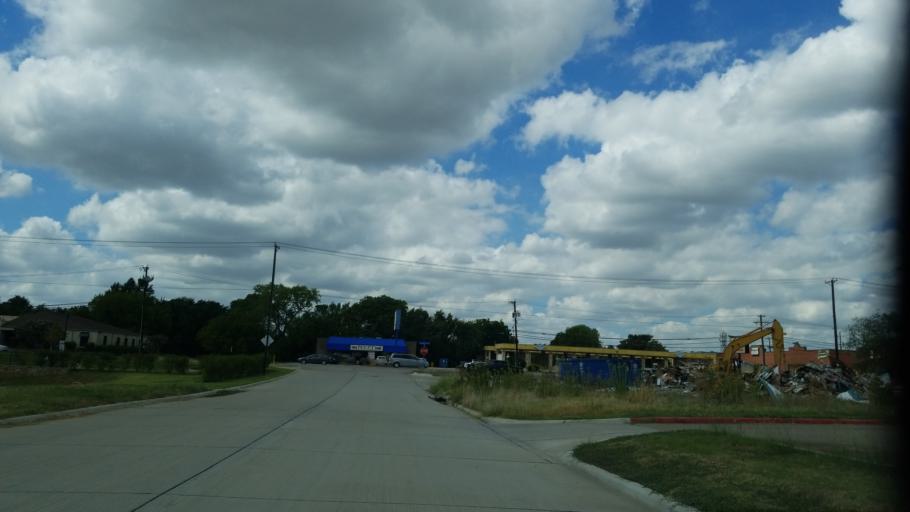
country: US
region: Texas
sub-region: Tarrant County
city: Euless
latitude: 32.8338
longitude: -97.0987
